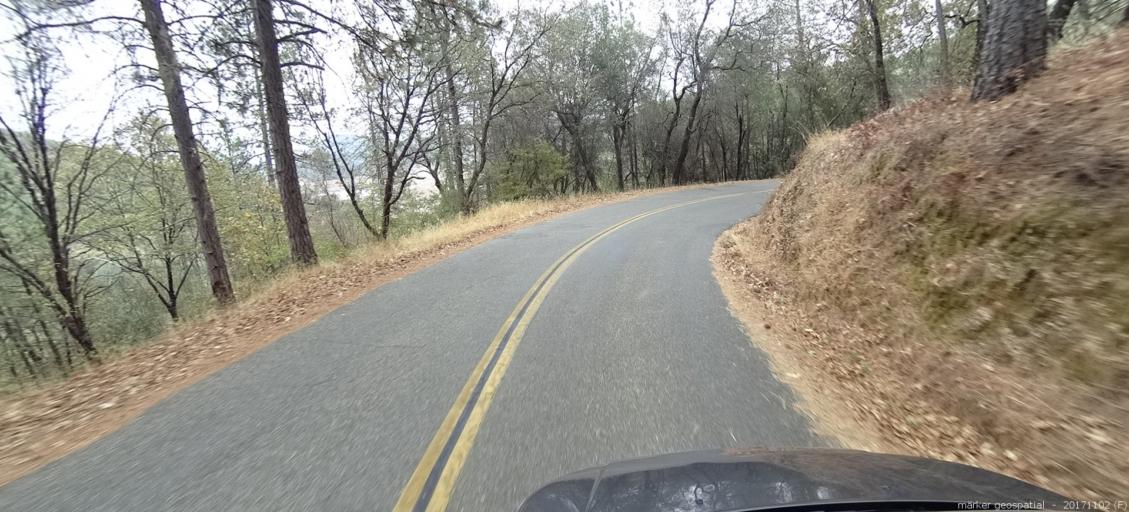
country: US
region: California
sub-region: Shasta County
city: Bella Vista
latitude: 40.7314
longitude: -122.2375
